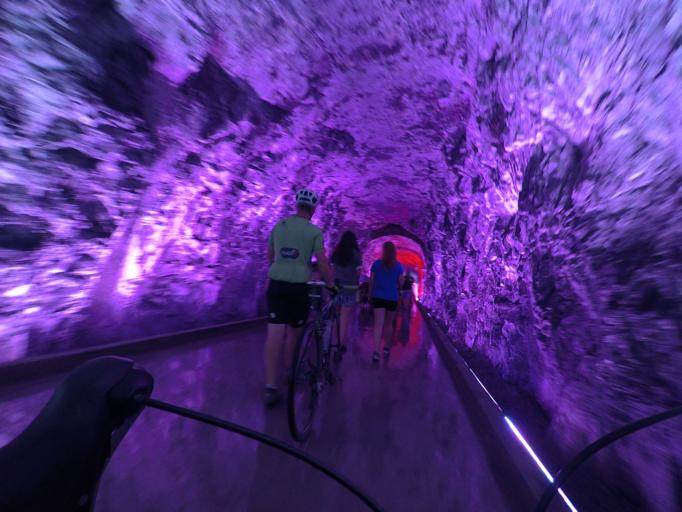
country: CA
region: Ontario
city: Brockville
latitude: 44.5915
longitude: -75.6843
